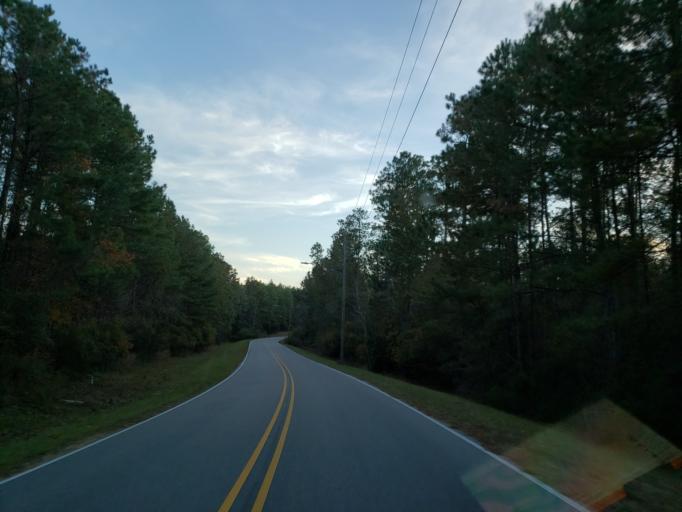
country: US
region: Mississippi
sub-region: Forrest County
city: Hattiesburg
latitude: 31.2713
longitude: -89.3097
